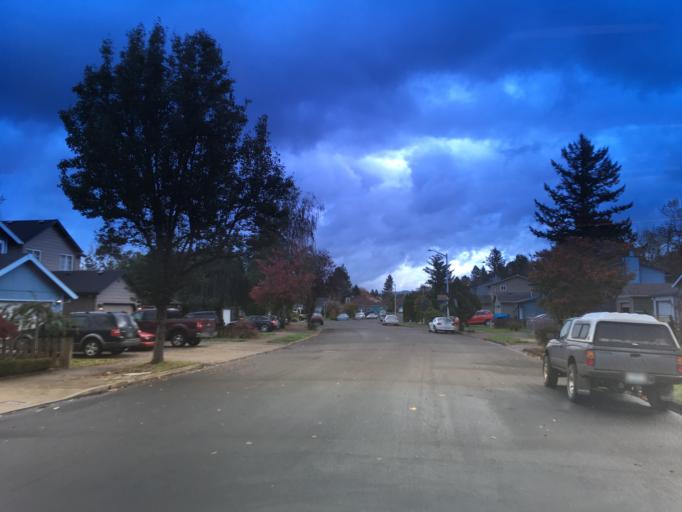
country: US
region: Oregon
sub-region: Multnomah County
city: Troutdale
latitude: 45.5169
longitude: -122.3869
